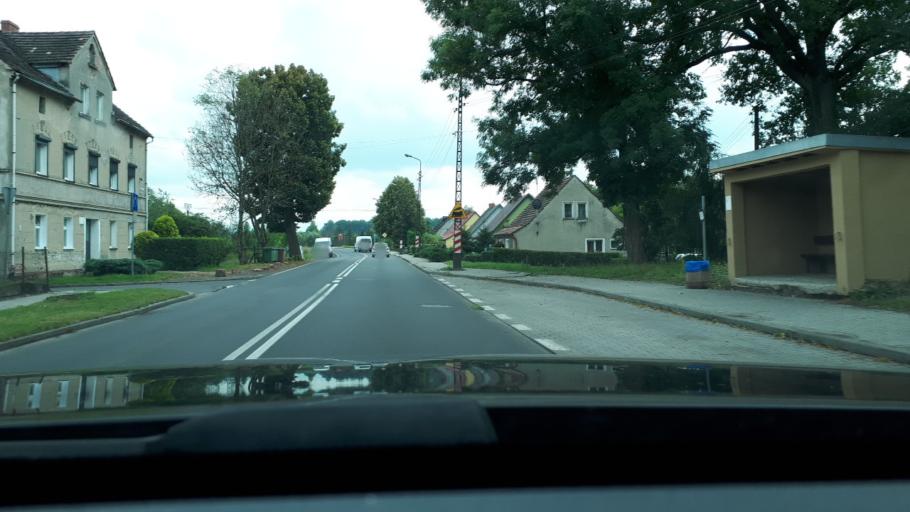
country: PL
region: Lower Silesian Voivodeship
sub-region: Powiat lubanski
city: Luban
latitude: 51.1010
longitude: 15.2941
